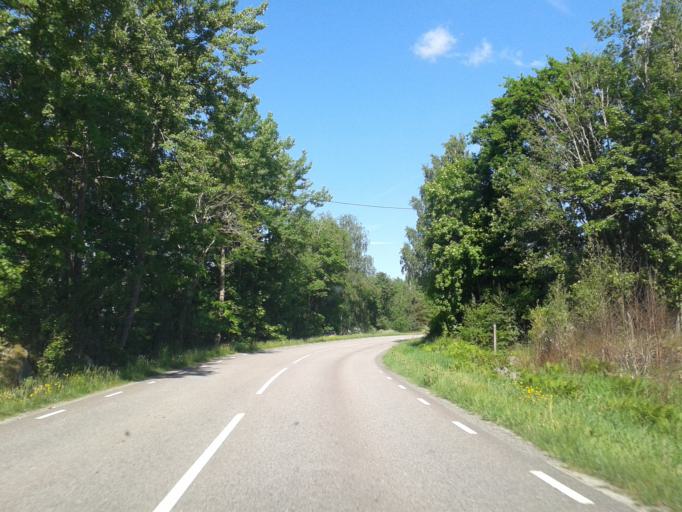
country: SE
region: Vaestra Goetaland
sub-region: Kungalvs Kommun
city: Kode
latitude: 57.9240
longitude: 11.9108
